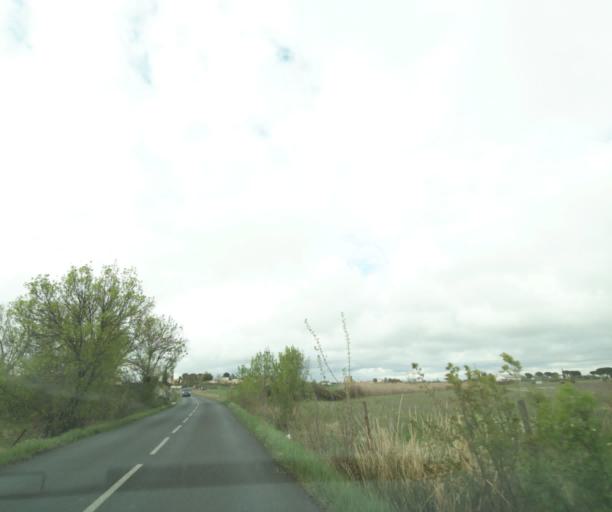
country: FR
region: Languedoc-Roussillon
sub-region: Departement de l'Herault
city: Saussan
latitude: 43.5619
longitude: 3.7757
